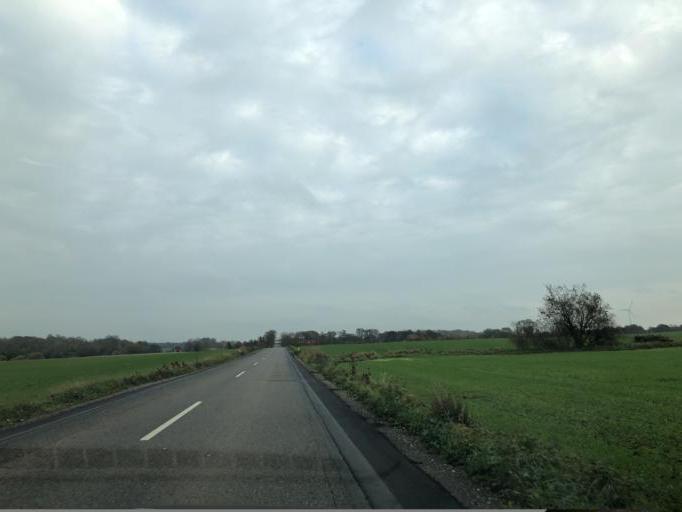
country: DK
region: Central Jutland
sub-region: Hedensted Kommune
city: Hornsyld
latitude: 55.7364
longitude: 9.7829
